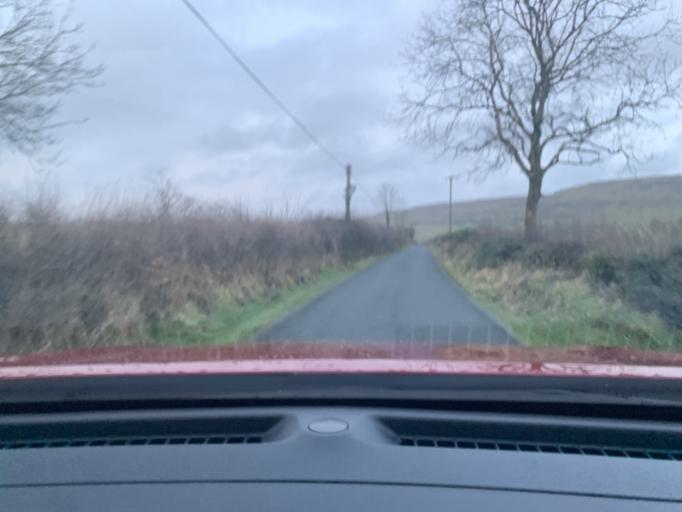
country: IE
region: Connaught
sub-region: Sligo
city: Ballymote
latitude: 54.0320
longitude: -8.4116
